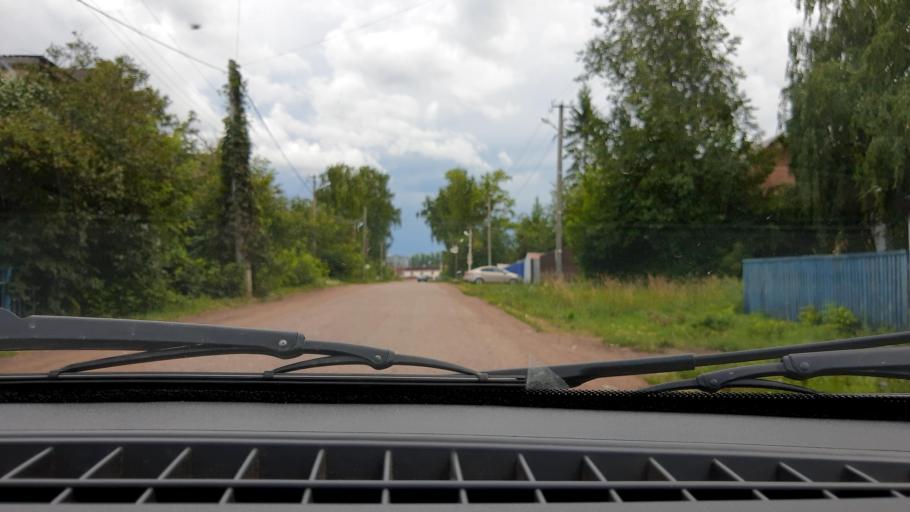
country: RU
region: Bashkortostan
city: Mikhaylovka
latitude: 54.8639
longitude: 55.8160
